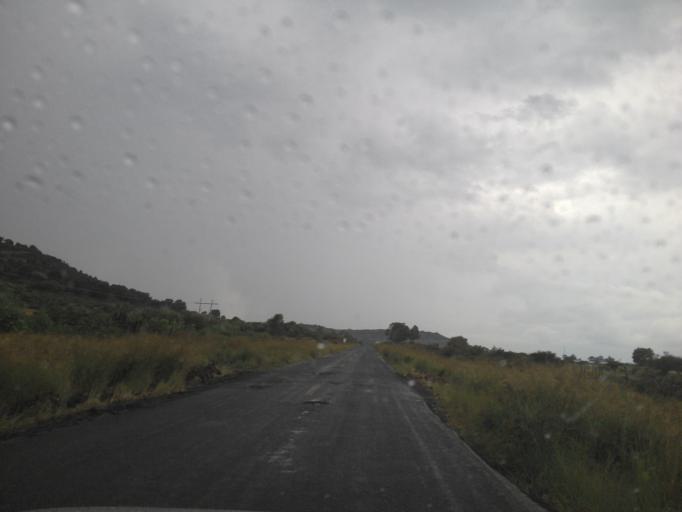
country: MX
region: Jalisco
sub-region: Arandas
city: Santiaguito (Santiaguito de Velazquez)
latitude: 20.7908
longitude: -102.2617
